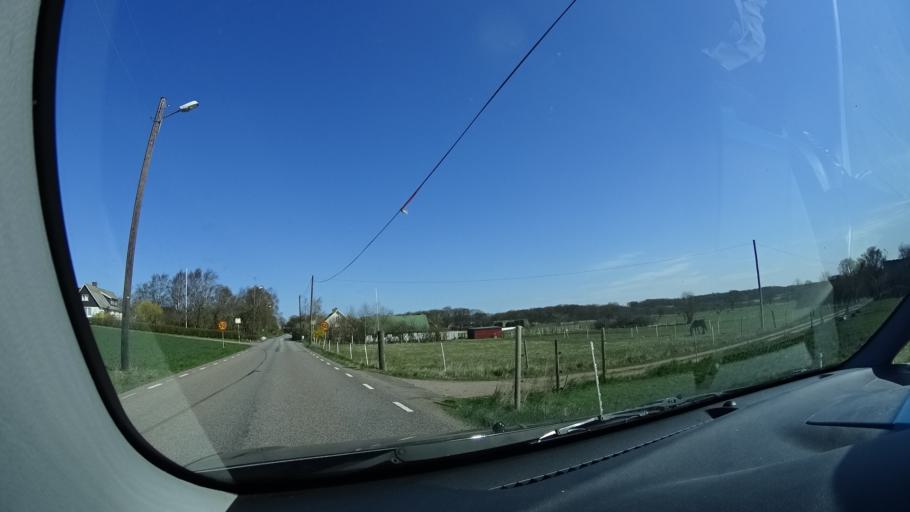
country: SE
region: Skane
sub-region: Hoganas Kommun
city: Hoganas
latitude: 56.2553
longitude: 12.5708
